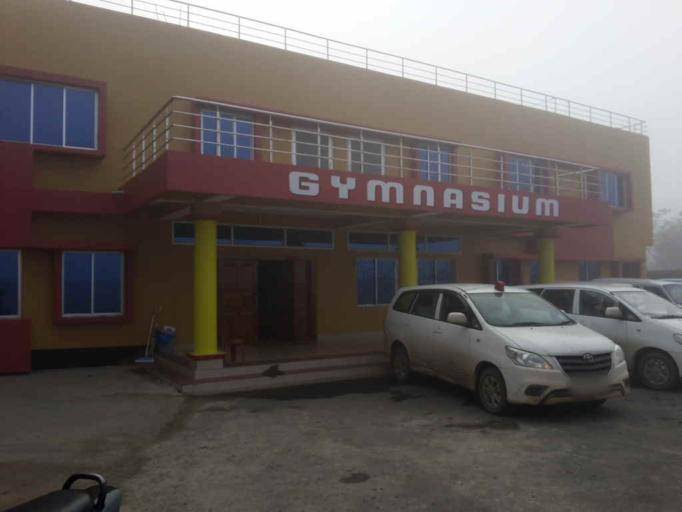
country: IN
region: Manipur
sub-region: Imphal East
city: Imphal
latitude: 24.8228
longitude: 93.8975
